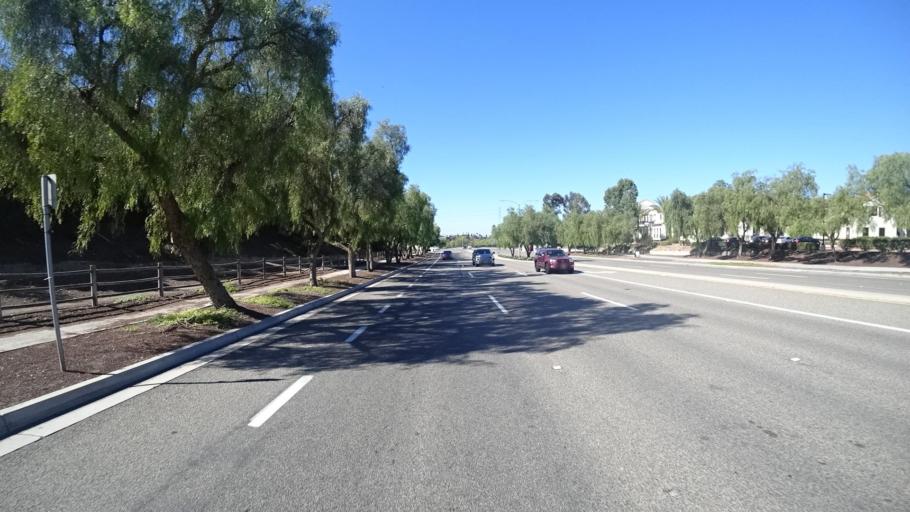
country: US
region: California
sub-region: San Diego County
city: La Presa
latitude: 32.6621
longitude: -116.9698
